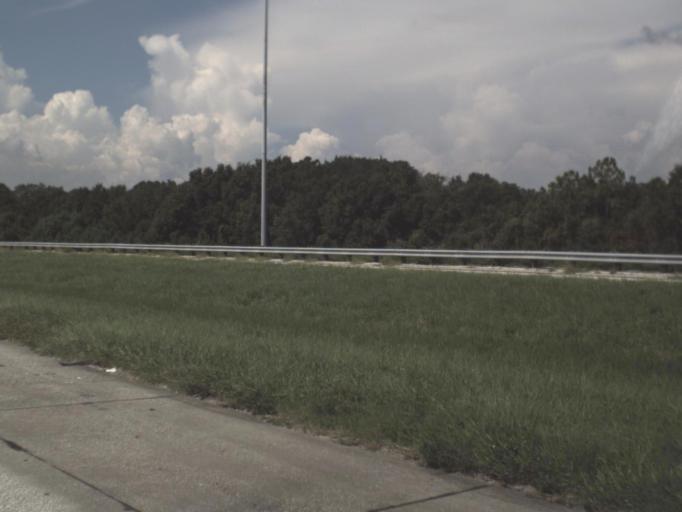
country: US
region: Florida
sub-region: Hillsborough County
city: Brandon
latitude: 27.9403
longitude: -82.3298
